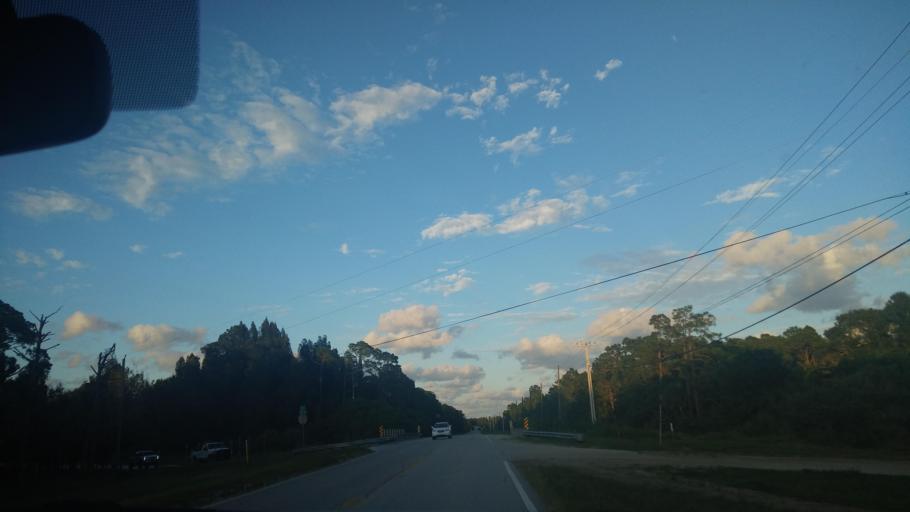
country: US
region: Florida
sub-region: Indian River County
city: Fellsmere
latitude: 27.7609
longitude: -80.6150
